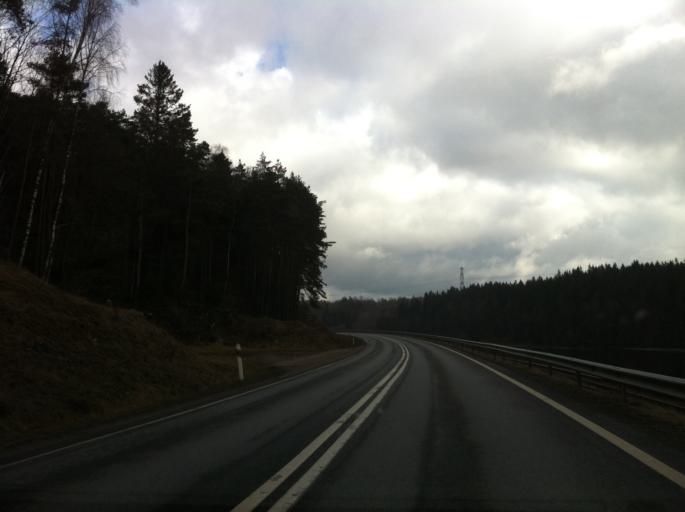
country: SE
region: Halland
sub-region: Halmstads Kommun
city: Oskarstrom
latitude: 56.8375
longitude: 12.9711
